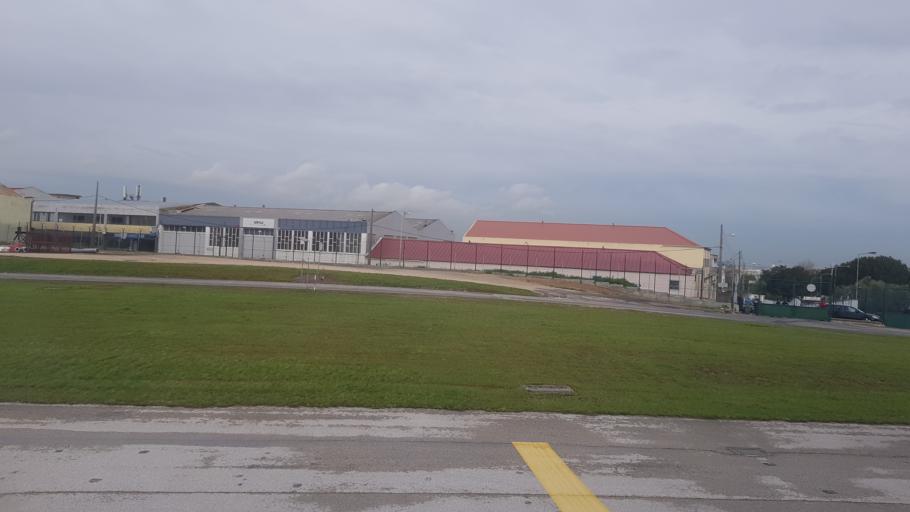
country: PT
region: Lisbon
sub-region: Loures
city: Camarate
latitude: 38.7846
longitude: -9.1321
